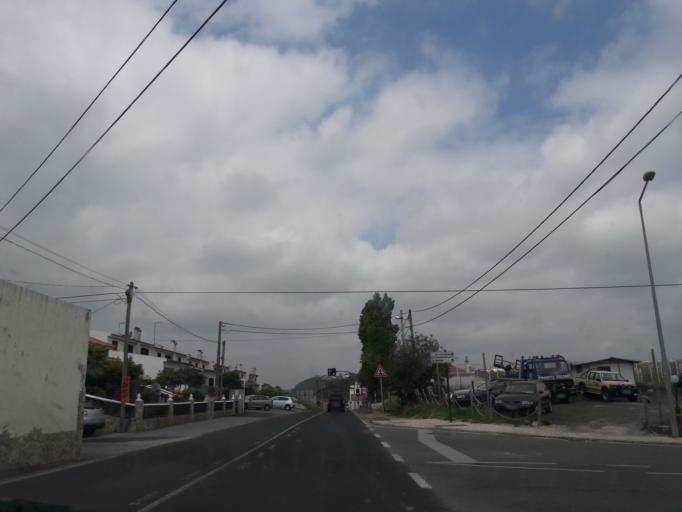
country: PT
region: Leiria
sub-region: Obidos
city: Obidos
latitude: 39.3441
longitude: -9.1680
